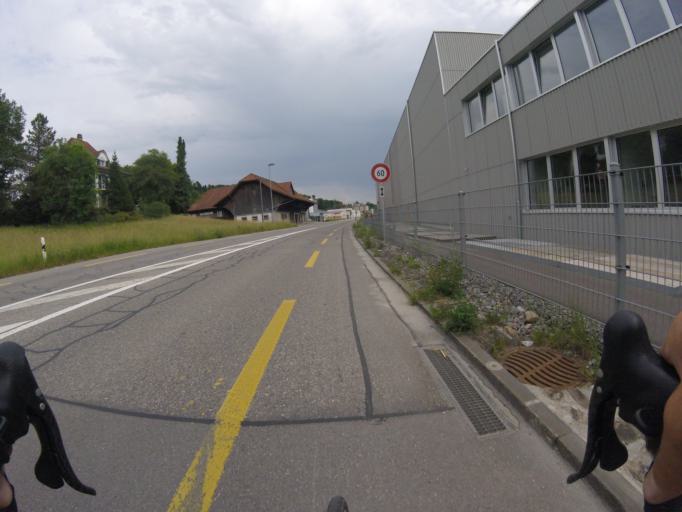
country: CH
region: Bern
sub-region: Seeland District
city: Lyss
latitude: 47.0658
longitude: 7.3308
